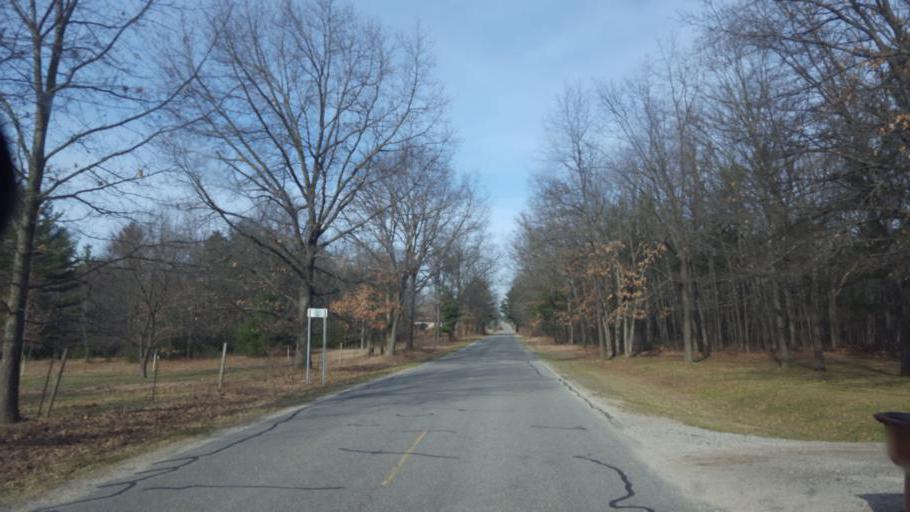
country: US
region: Michigan
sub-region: Montcalm County
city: Howard City
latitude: 43.5258
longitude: -85.5243
